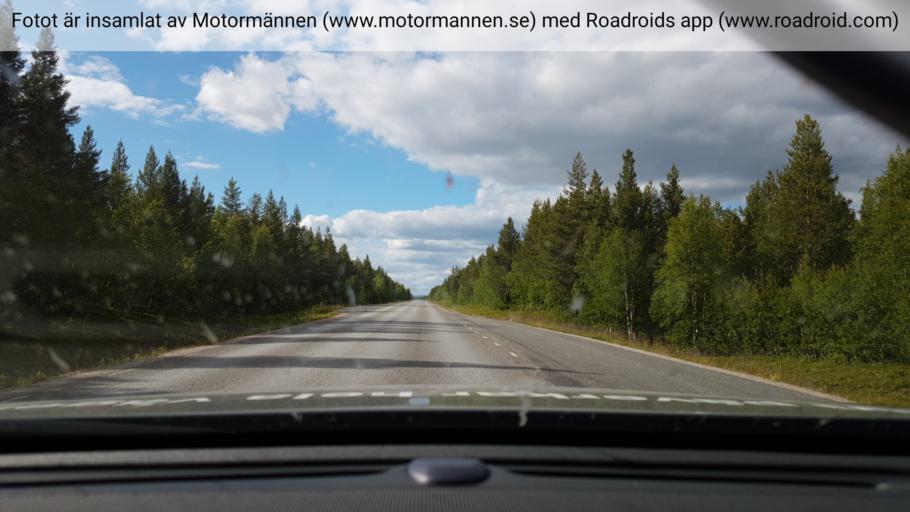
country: SE
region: Norrbotten
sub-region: Arjeplogs Kommun
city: Arjeplog
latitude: 66.1755
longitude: 17.3206
